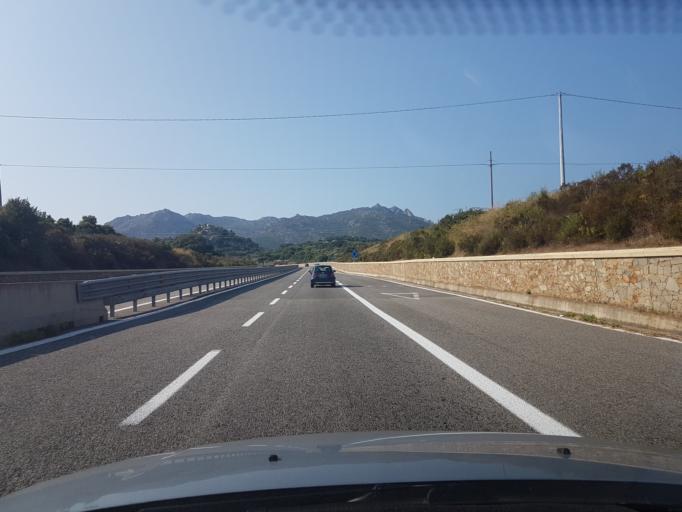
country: IT
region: Sardinia
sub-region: Provincia di Olbia-Tempio
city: Padru
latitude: 40.8042
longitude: 9.5910
